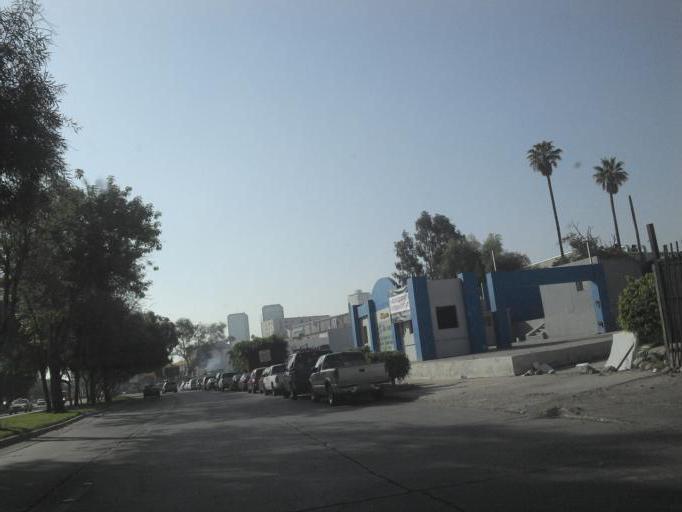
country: MX
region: Baja California
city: Tijuana
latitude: 32.5198
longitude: -117.0142
